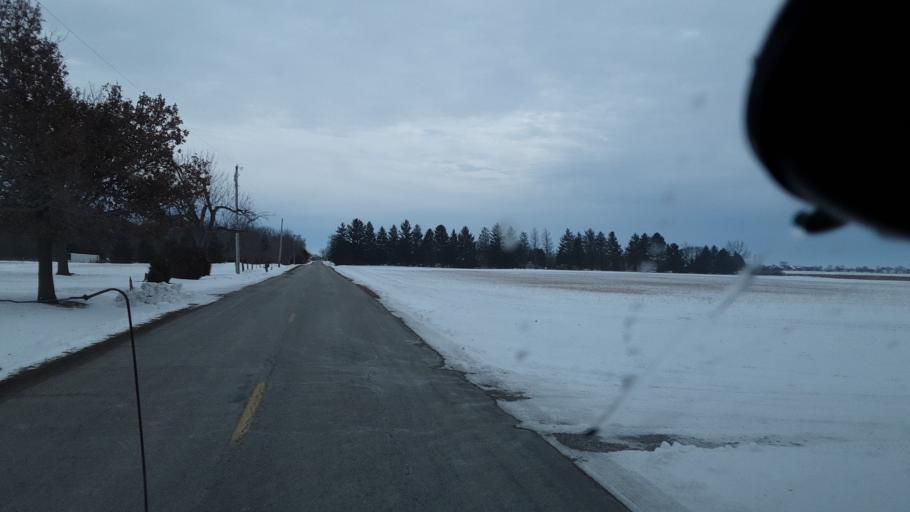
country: US
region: Ohio
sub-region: Madison County
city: Bethel
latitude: 39.7186
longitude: -83.3831
